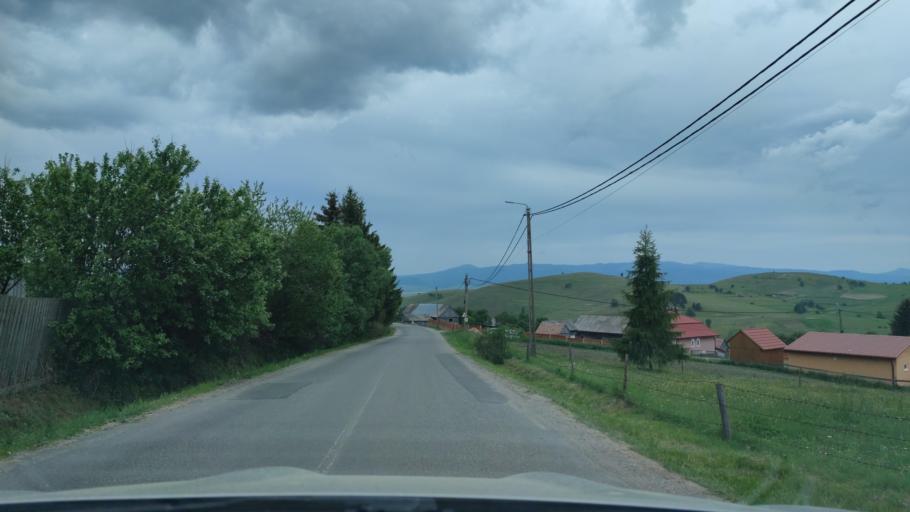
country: RO
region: Harghita
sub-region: Comuna Ditrau
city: Ditrau
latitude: 46.8533
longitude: 25.5073
